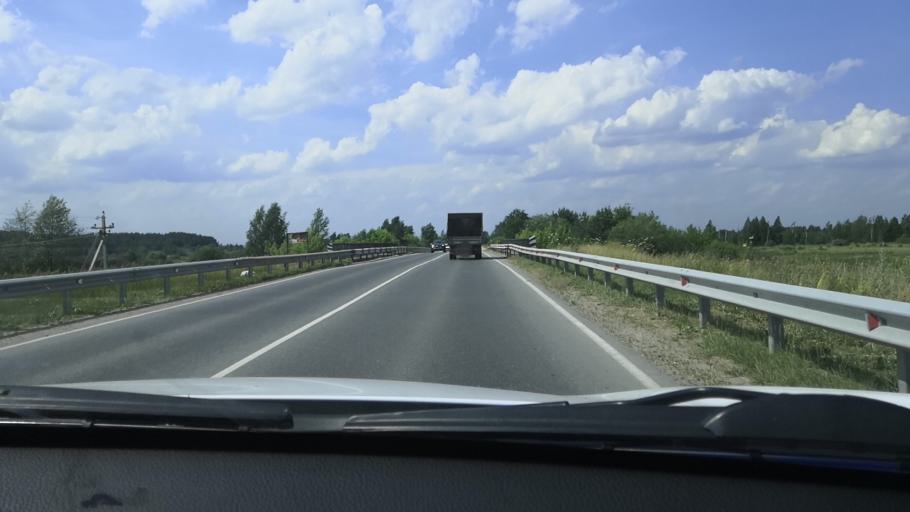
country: RU
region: Rjazan
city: Murmino
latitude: 54.6333
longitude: 39.9496
